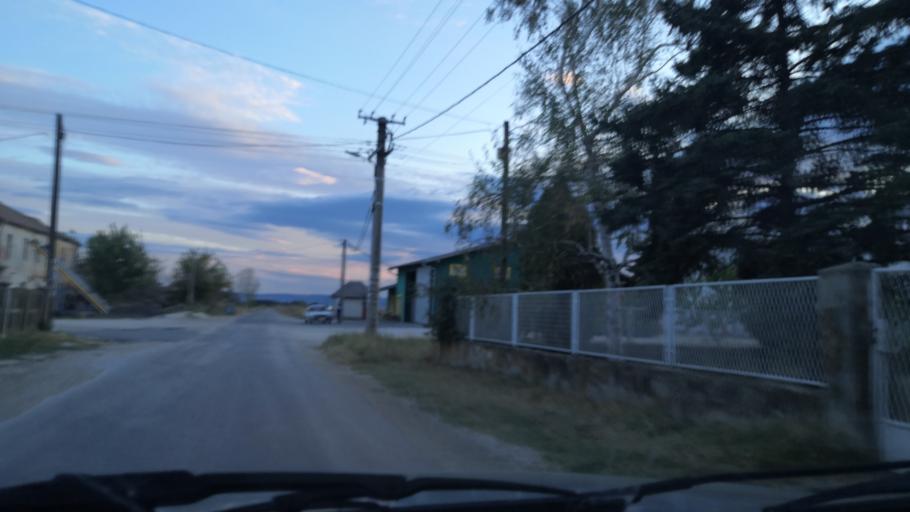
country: RO
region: Mehedinti
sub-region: Comuna Gogosu
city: Balta Verde
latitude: 44.2912
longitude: 22.5816
